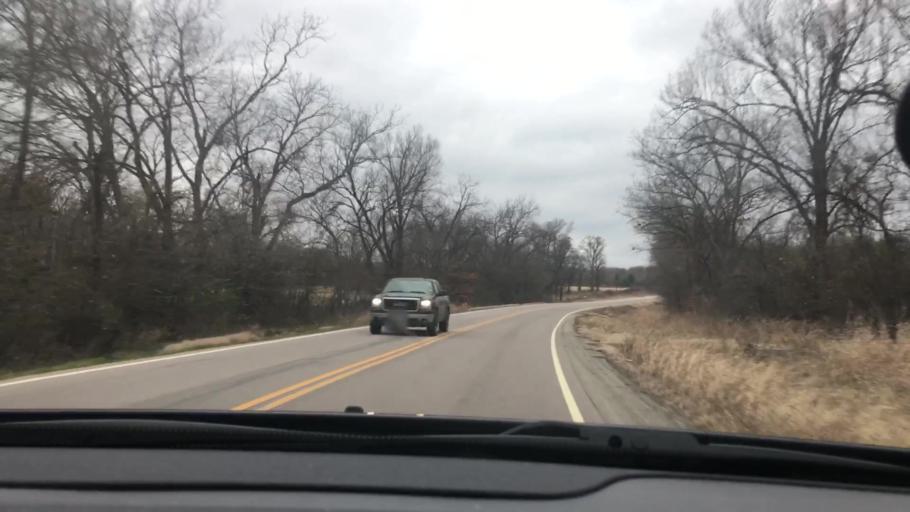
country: US
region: Oklahoma
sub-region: Atoka County
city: Atoka
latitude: 34.3667
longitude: -96.3329
